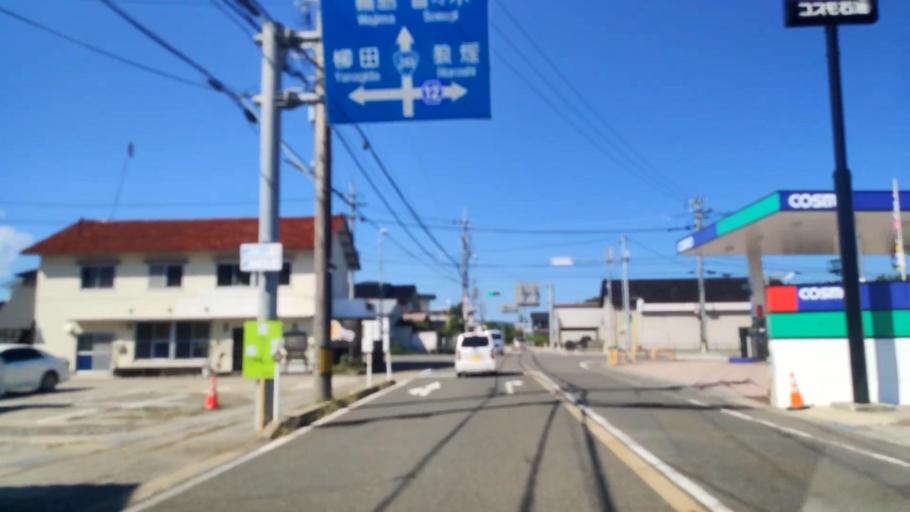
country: JP
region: Ishikawa
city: Nanao
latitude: 37.4434
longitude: 137.2645
